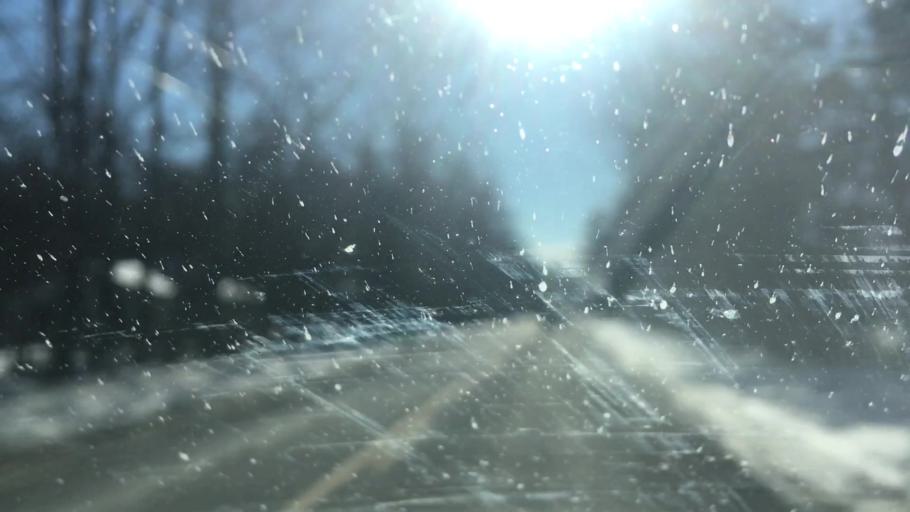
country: US
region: Maine
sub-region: Hancock County
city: Sedgwick
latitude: 44.3901
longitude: -68.6421
